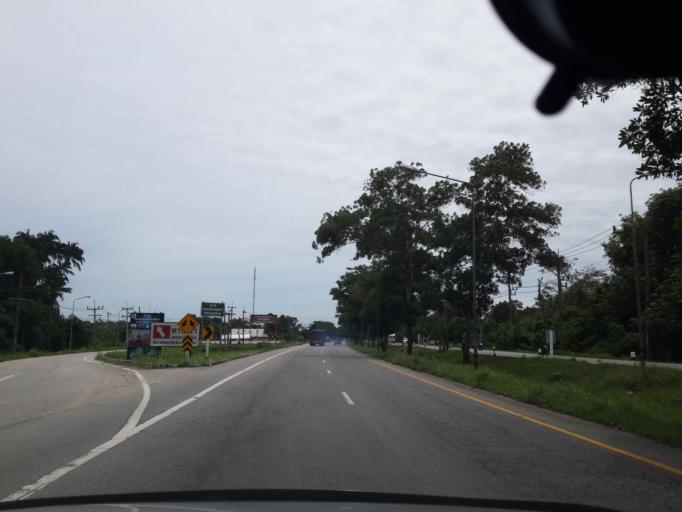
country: TH
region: Narathiwat
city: Yi-ngo
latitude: 6.4052
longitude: 101.7496
